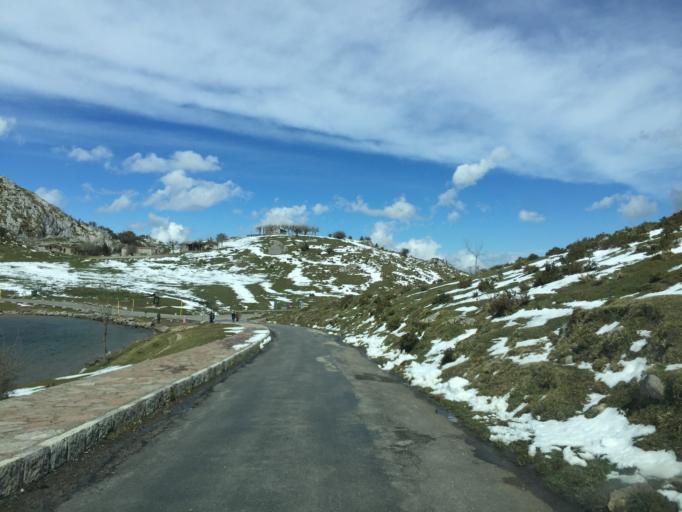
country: ES
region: Asturias
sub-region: Province of Asturias
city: Amieva
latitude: 43.2728
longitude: -4.9878
